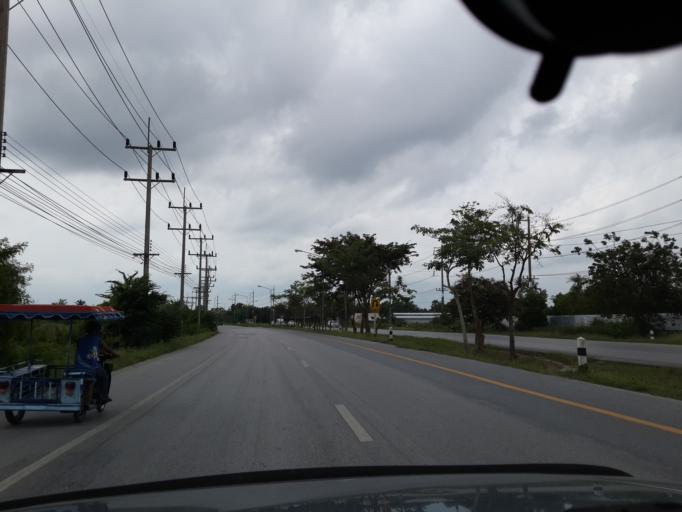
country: TH
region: Pattani
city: Pattani
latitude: 6.8687
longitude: 101.2760
